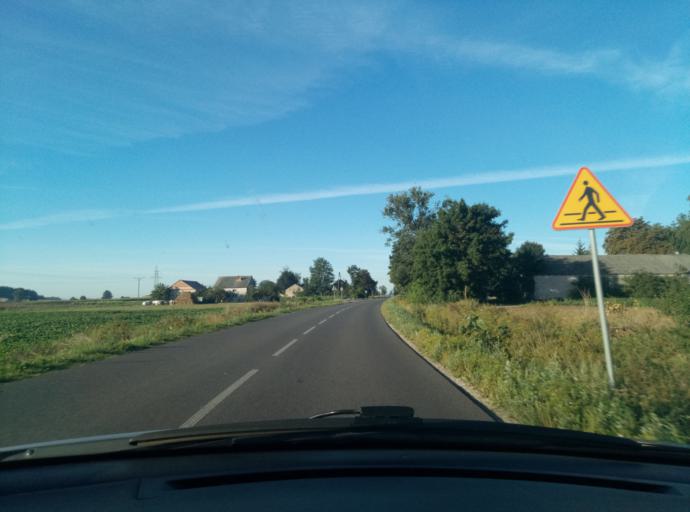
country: PL
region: Kujawsko-Pomorskie
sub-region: Powiat golubsko-dobrzynski
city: Kowalewo Pomorskie
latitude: 53.1898
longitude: 18.9109
